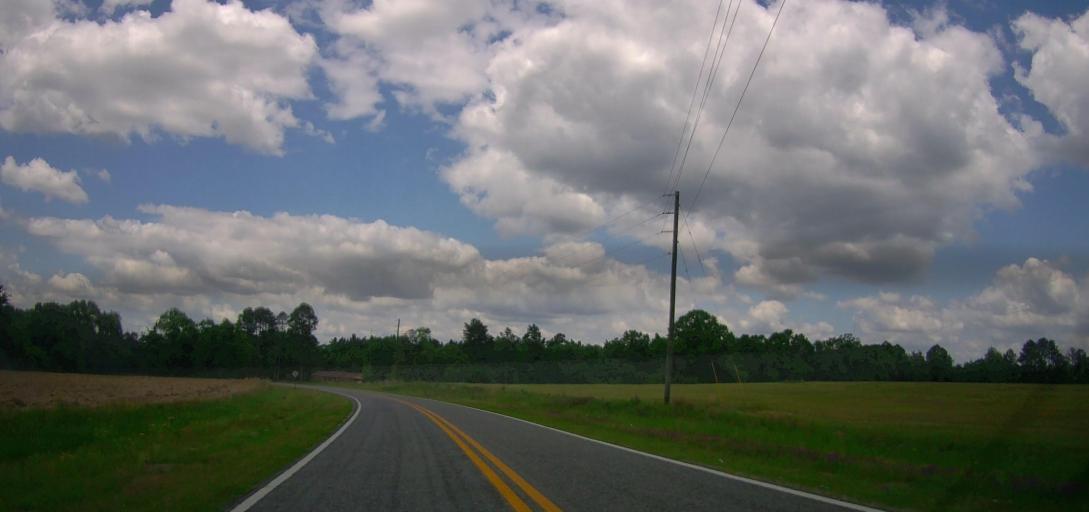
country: US
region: Georgia
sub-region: Laurens County
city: East Dublin
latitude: 32.5380
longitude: -82.8103
